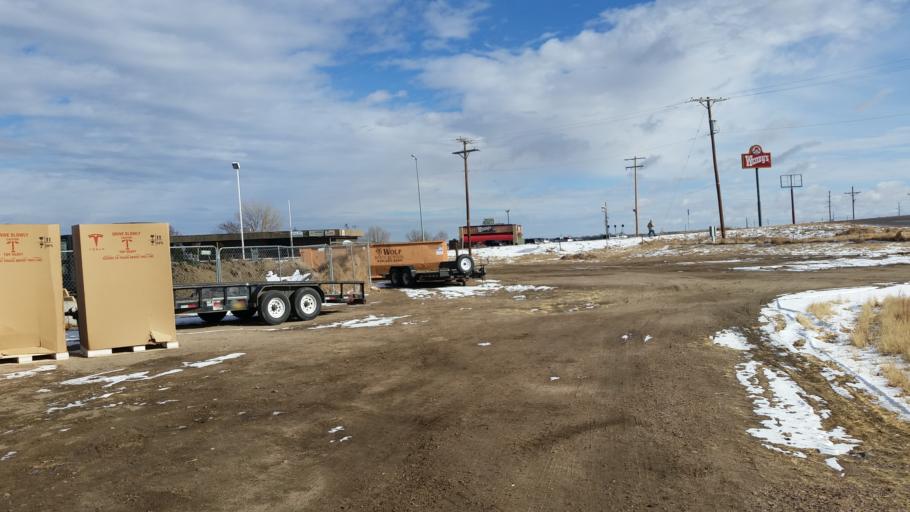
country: US
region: Colorado
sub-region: Morgan County
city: Brush
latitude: 40.2706
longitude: -103.6227
